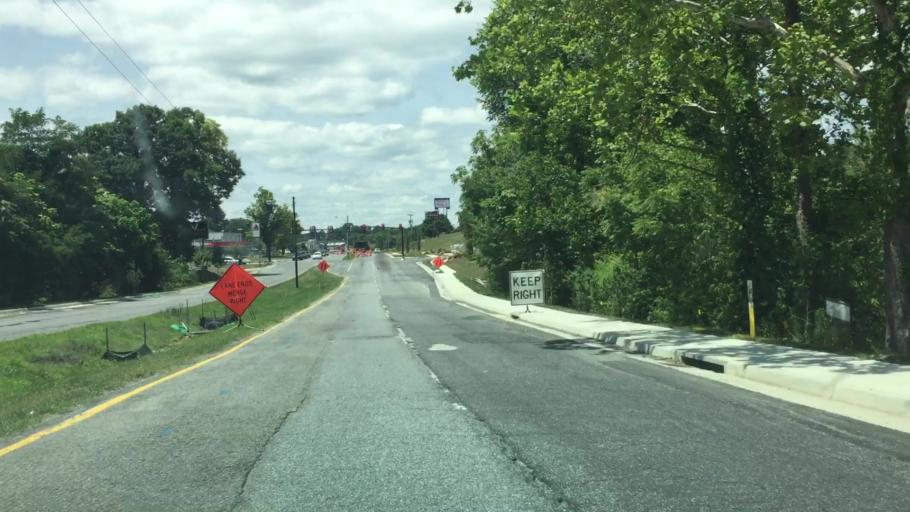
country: US
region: Virginia
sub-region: Wythe County
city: Wytheville
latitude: 36.9484
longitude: -81.0628
